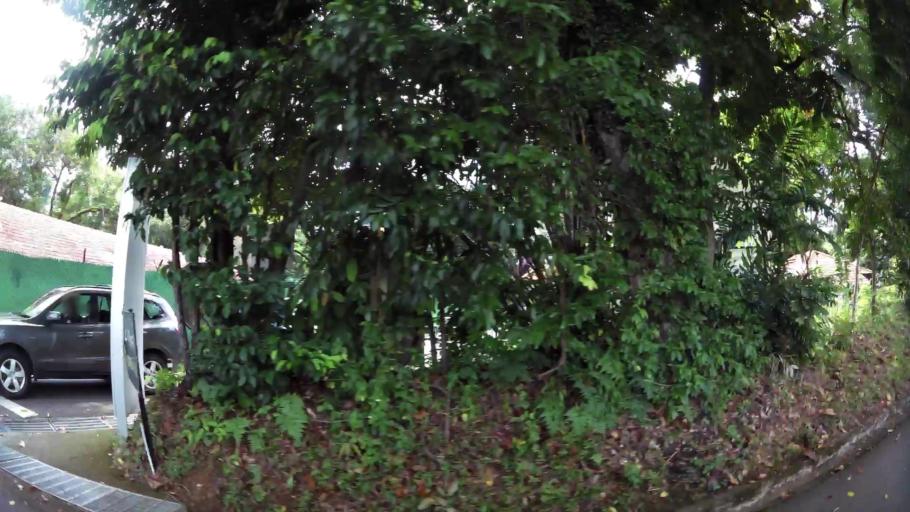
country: SG
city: Singapore
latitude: 1.3031
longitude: 103.8115
